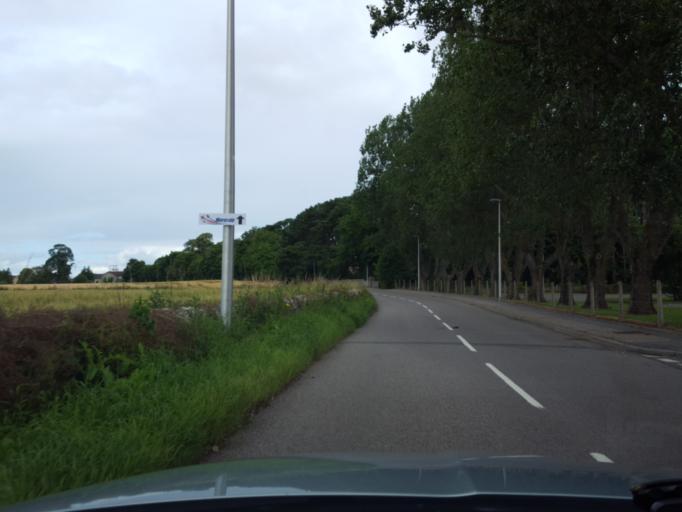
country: GB
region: Scotland
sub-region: Moray
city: Kinloss
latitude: 57.6336
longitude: -3.5615
